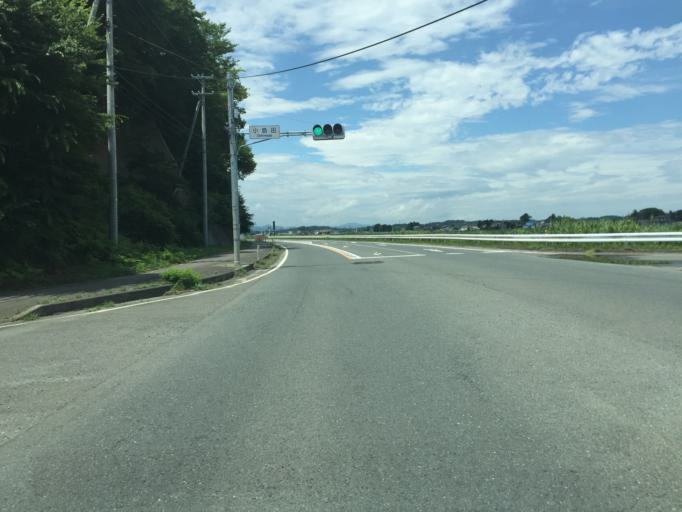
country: JP
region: Fukushima
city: Namie
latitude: 37.6864
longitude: 140.9800
